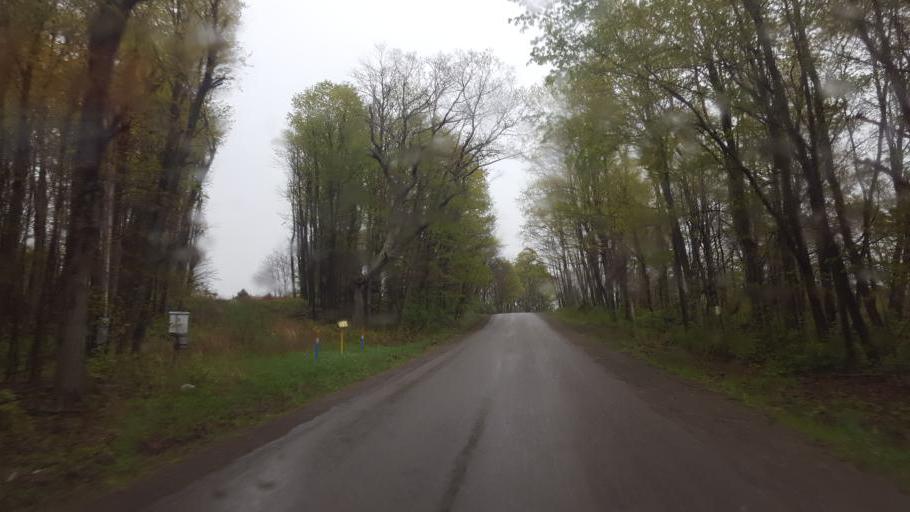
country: US
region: Pennsylvania
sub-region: Tioga County
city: Elkland
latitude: 42.0680
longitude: -77.3711
